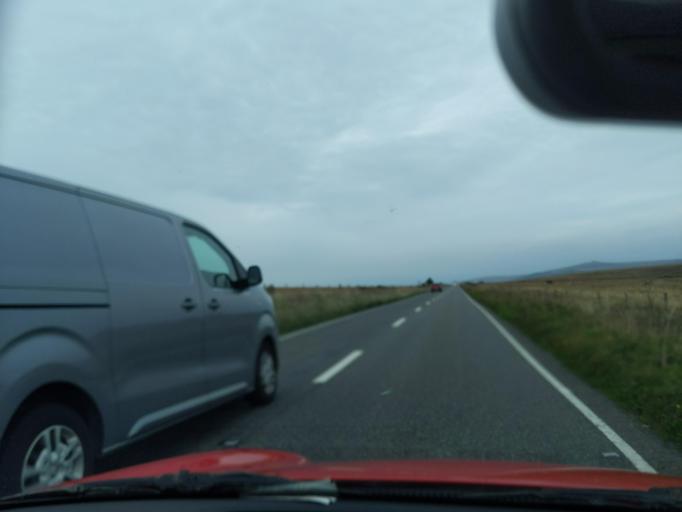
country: GB
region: England
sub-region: Devon
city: Tavistock
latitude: 50.6159
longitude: -4.1067
